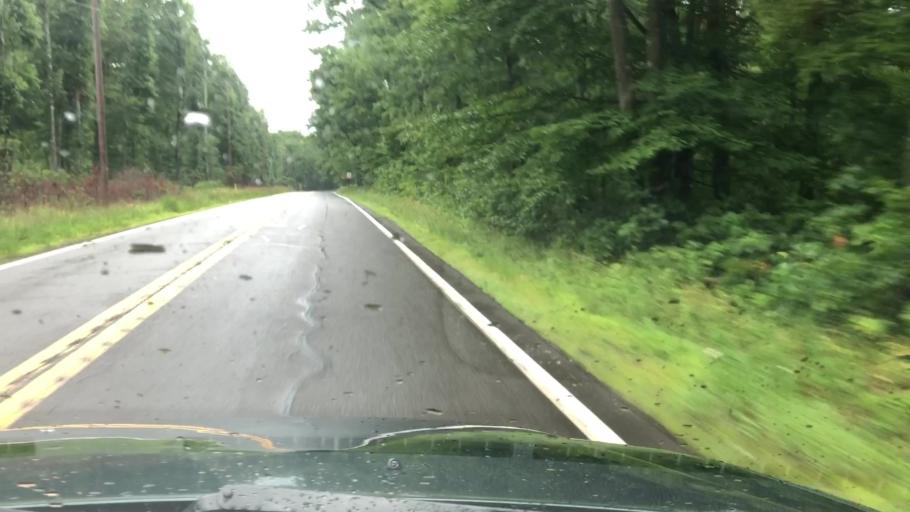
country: US
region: Pennsylvania
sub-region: Wayne County
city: Hawley
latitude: 41.3467
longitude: -75.2127
